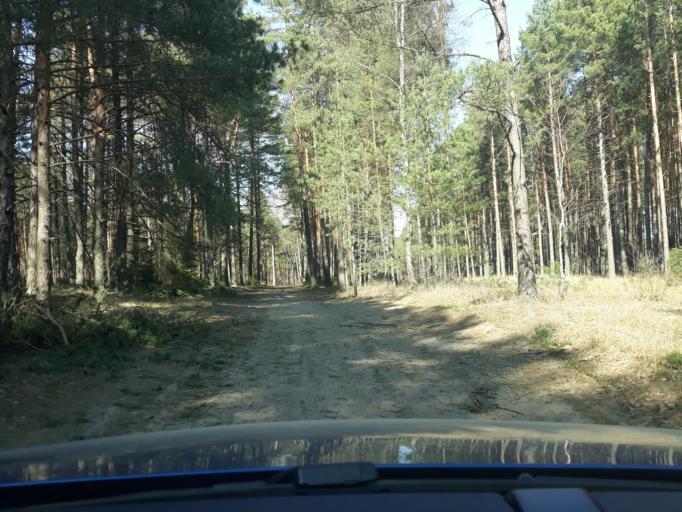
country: PL
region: Pomeranian Voivodeship
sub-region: Powiat bytowski
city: Lipnica
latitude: 53.8630
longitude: 17.4289
